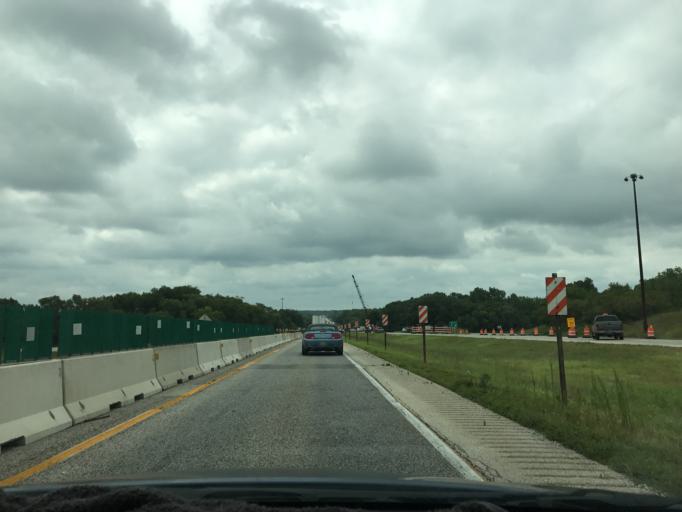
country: US
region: Illinois
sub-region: Henry County
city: Colona
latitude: 41.4905
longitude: -90.3386
